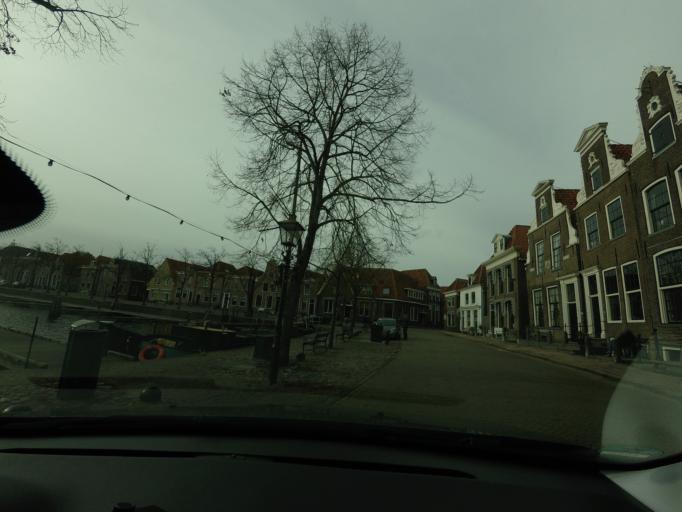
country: NL
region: Overijssel
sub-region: Gemeente Steenwijkerland
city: Blokzijl
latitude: 52.7273
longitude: 5.9596
